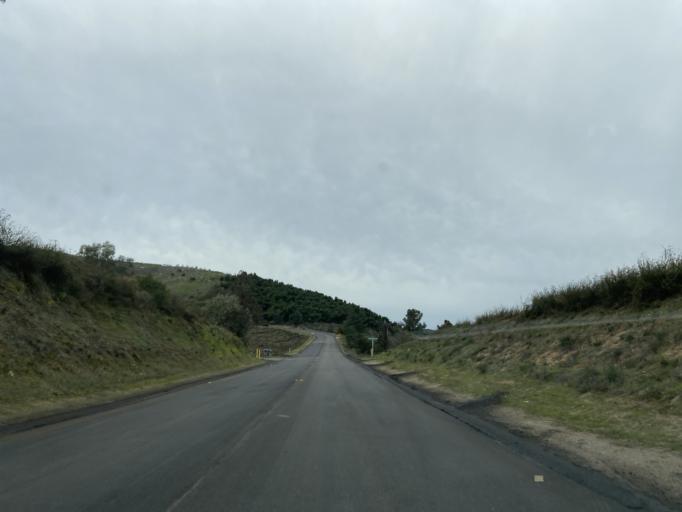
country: US
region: California
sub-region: San Diego County
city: Valley Center
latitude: 33.3082
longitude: -117.0155
